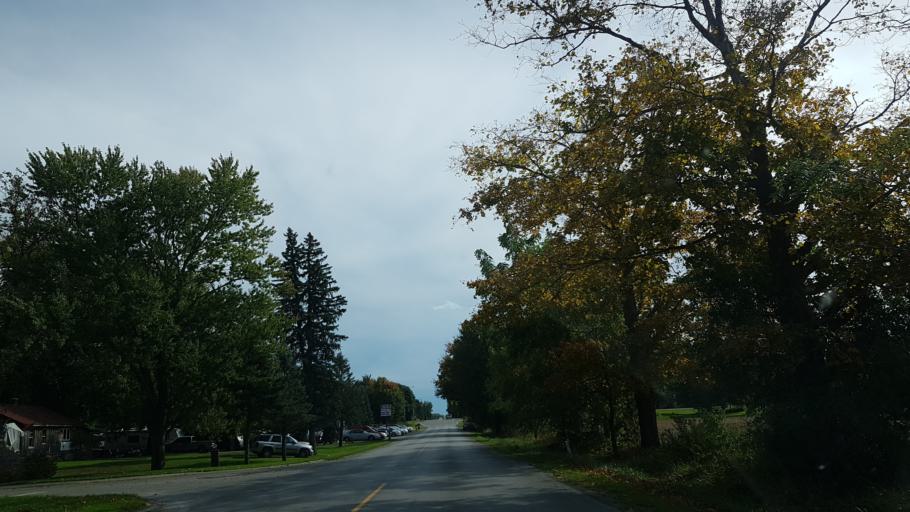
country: CA
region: Ontario
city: Delaware
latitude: 43.0017
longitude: -81.3967
